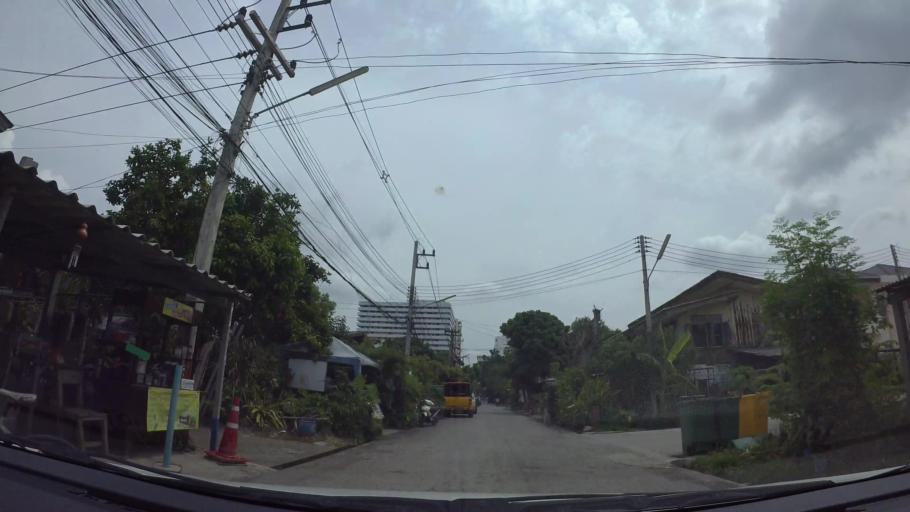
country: TH
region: Chiang Mai
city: Chiang Mai
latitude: 18.7869
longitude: 98.9754
